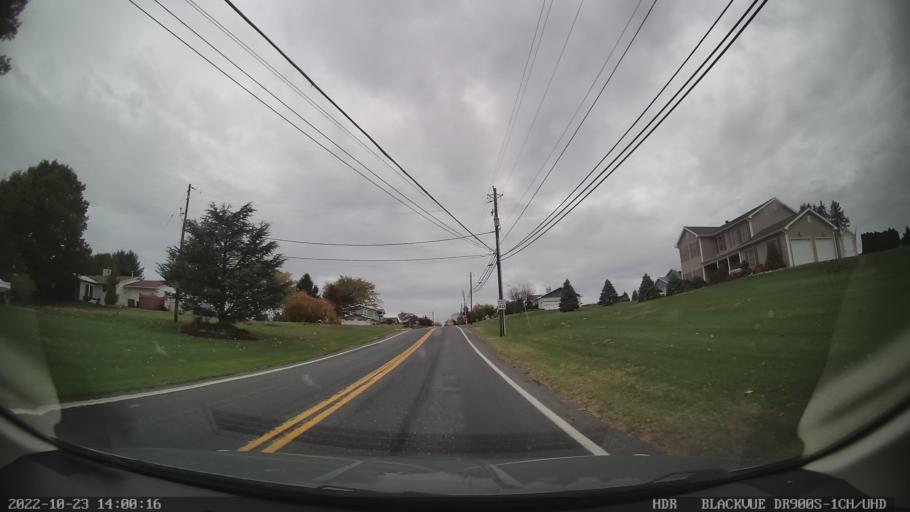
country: US
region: Pennsylvania
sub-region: Northampton County
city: Northampton
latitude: 40.7141
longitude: -75.4828
